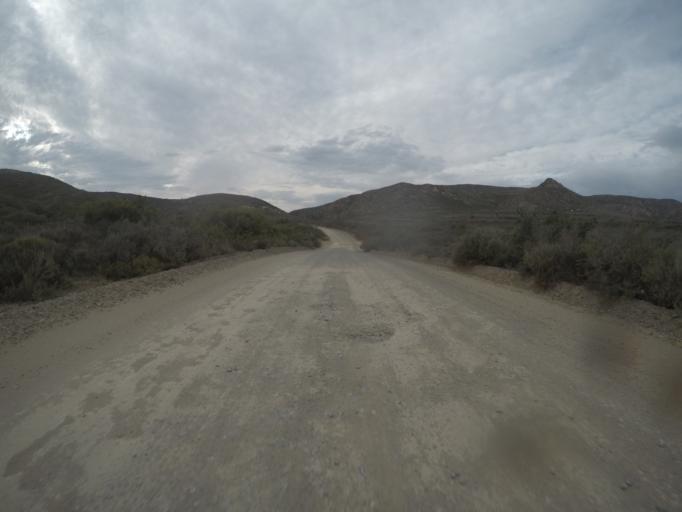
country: ZA
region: Eastern Cape
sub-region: Cacadu District Municipality
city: Willowmore
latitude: -33.4986
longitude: 23.6371
